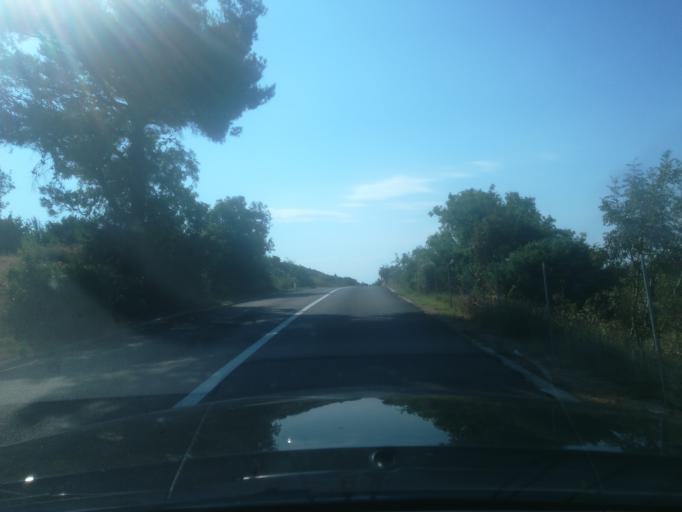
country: HR
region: Primorsko-Goranska
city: Banjol
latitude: 44.7232
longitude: 14.8206
